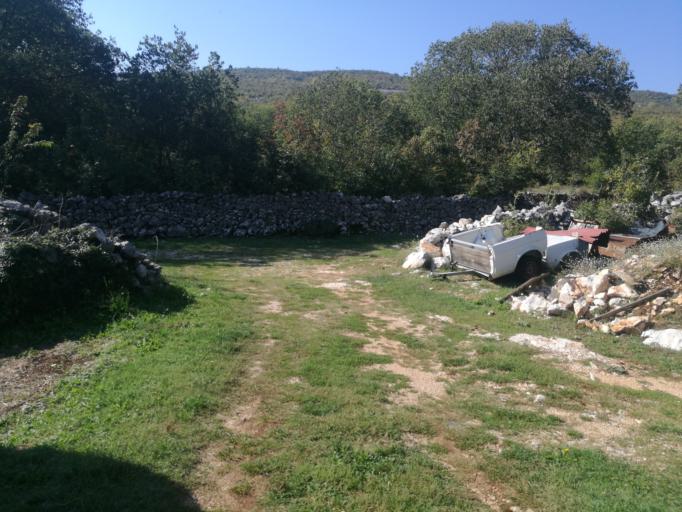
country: HR
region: Splitsko-Dalmatinska
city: Trilj
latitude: 43.5390
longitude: 16.7283
